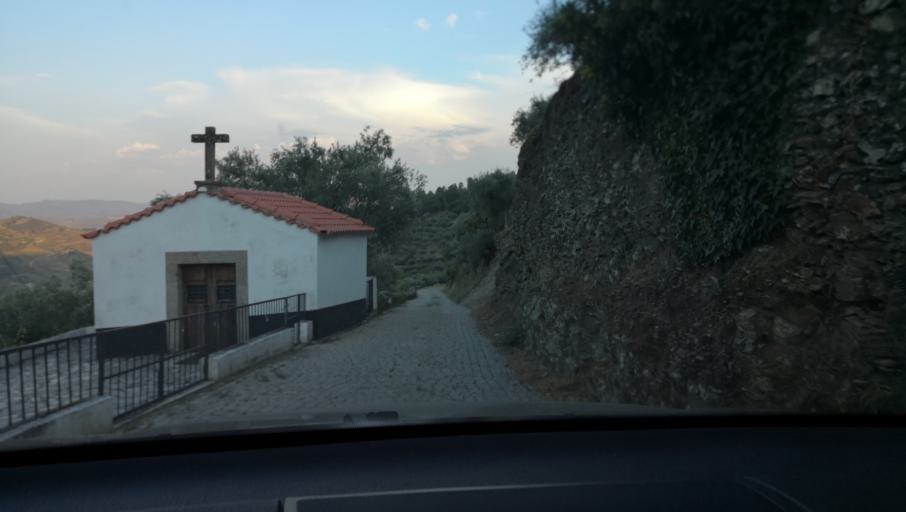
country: PT
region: Vila Real
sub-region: Sabrosa
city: Vilela
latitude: 41.1954
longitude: -7.5712
